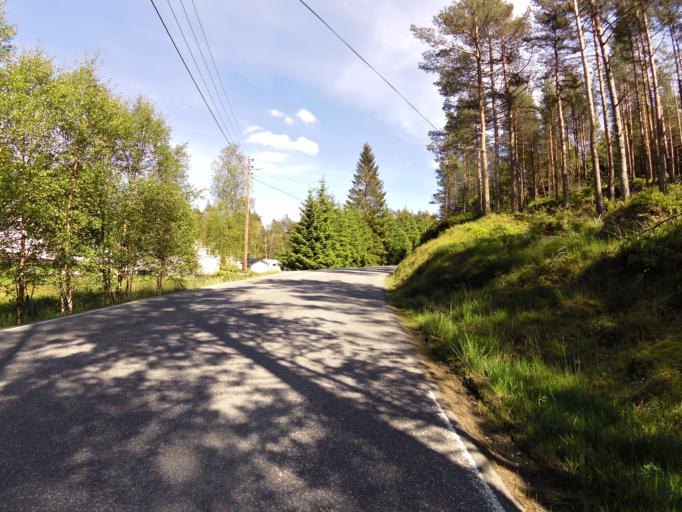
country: NO
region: Hordaland
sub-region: Stord
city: Sagvag
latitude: 59.7904
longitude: 5.4367
